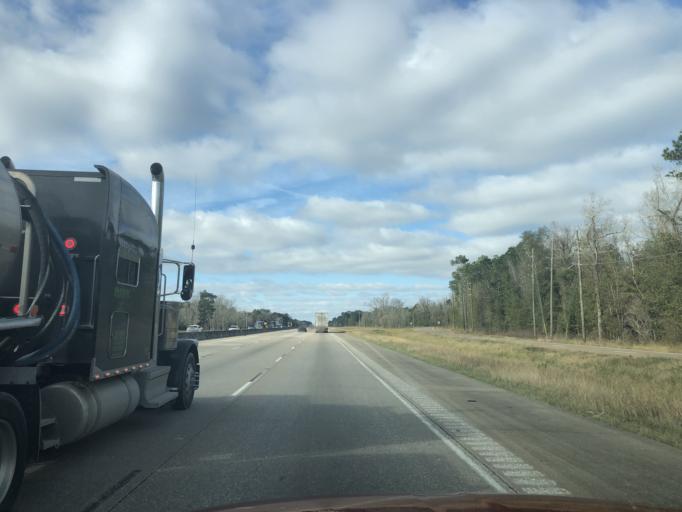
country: US
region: Texas
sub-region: Chambers County
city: Anahuac
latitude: 29.8386
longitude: -94.6064
